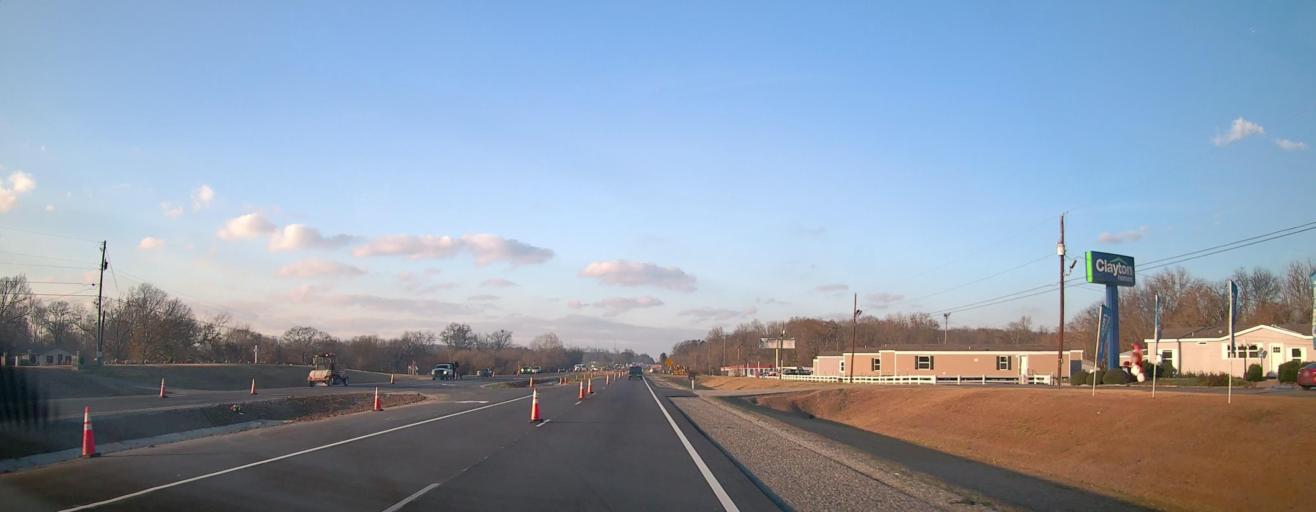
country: US
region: Alabama
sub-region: Calhoun County
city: Alexandria
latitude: 33.7326
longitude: -85.8795
